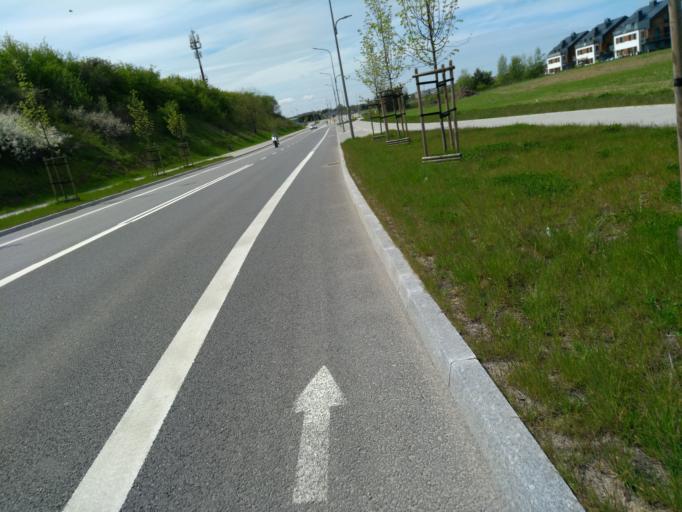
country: PL
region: Pomeranian Voivodeship
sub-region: Gdynia
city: Wielki Kack
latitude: 54.4165
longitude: 18.4723
